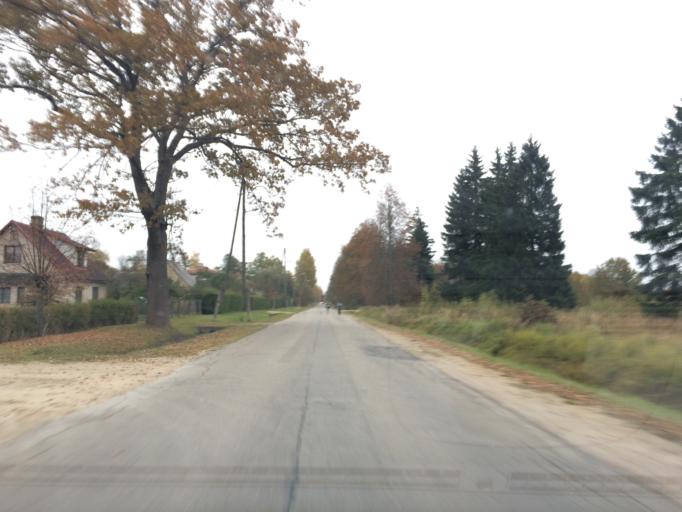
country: LV
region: Plavinu
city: Plavinas
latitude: 56.6188
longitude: 25.7526
